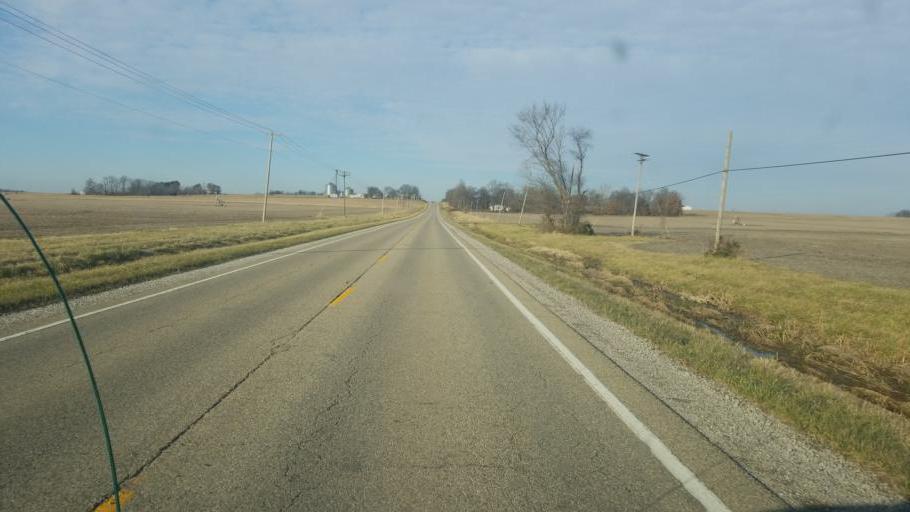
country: US
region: Illinois
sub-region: Lawrence County
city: Lawrenceville
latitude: 38.6494
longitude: -87.6943
